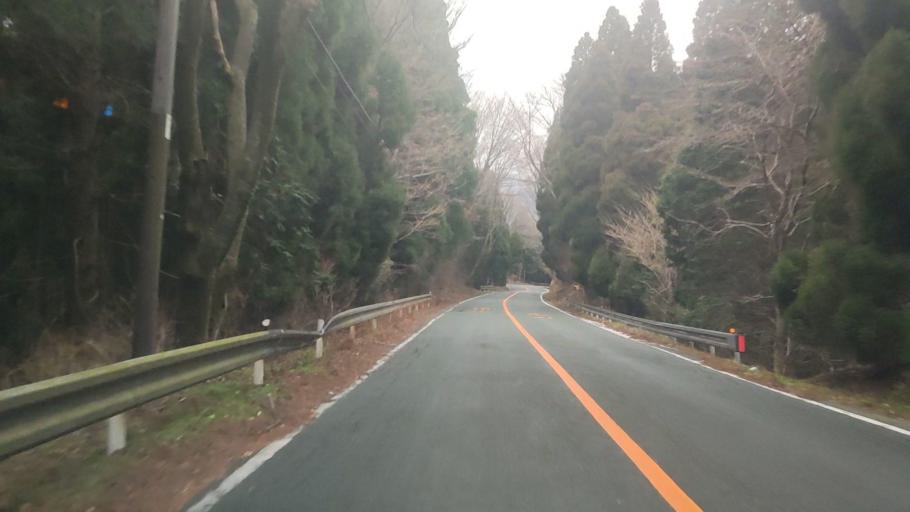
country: JP
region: Kumamoto
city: Aso
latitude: 32.8792
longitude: 131.1743
